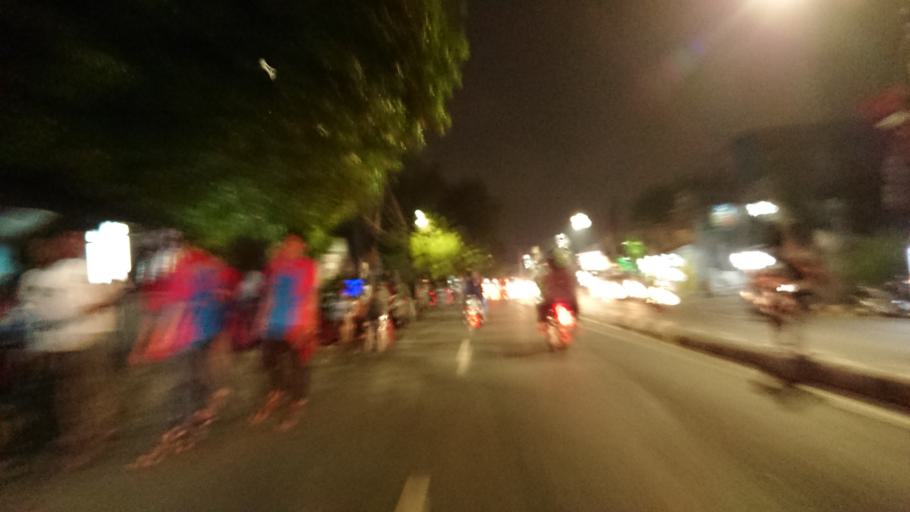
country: ID
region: Jakarta Raya
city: Jakarta
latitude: -6.1936
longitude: 106.8053
